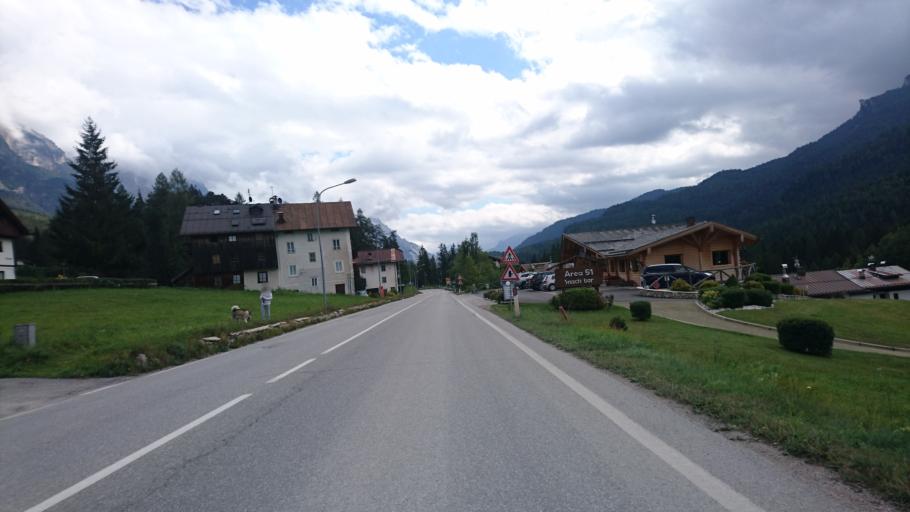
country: IT
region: Veneto
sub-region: Provincia di Belluno
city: Cortina d'Ampezzo
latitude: 46.5069
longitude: 12.1582
